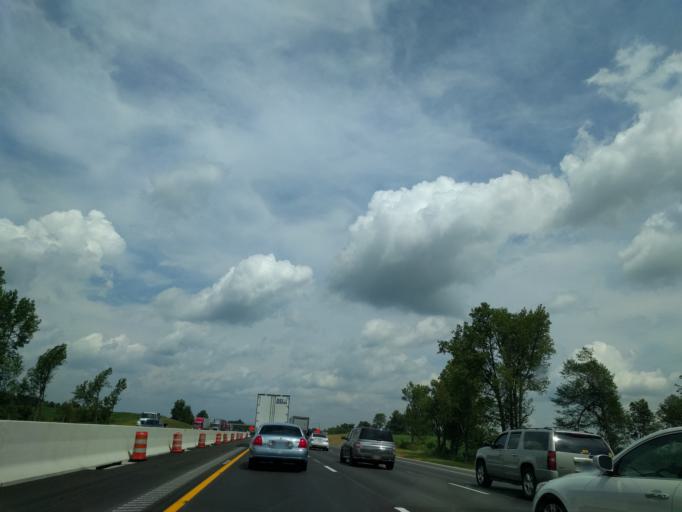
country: US
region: Kentucky
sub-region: Larue County
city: Hodgenville
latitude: 37.5347
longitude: -85.8820
